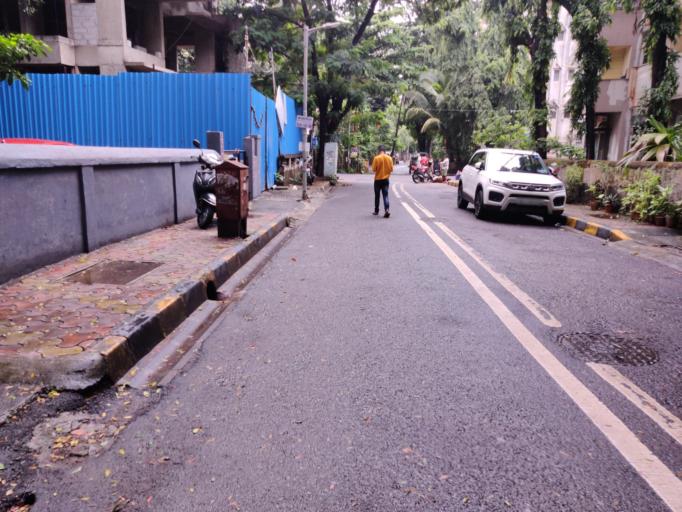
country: IN
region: Maharashtra
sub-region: Mumbai Suburban
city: Borivli
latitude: 19.2517
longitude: 72.8575
